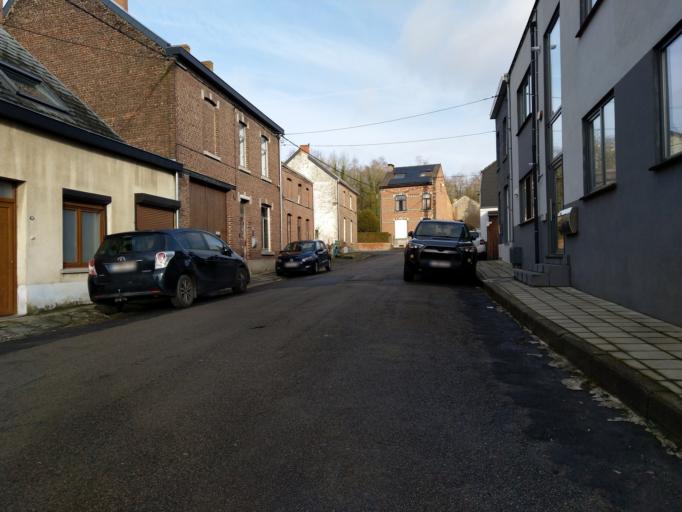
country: BE
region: Wallonia
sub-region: Province du Hainaut
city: Mons
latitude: 50.4903
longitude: 3.9647
